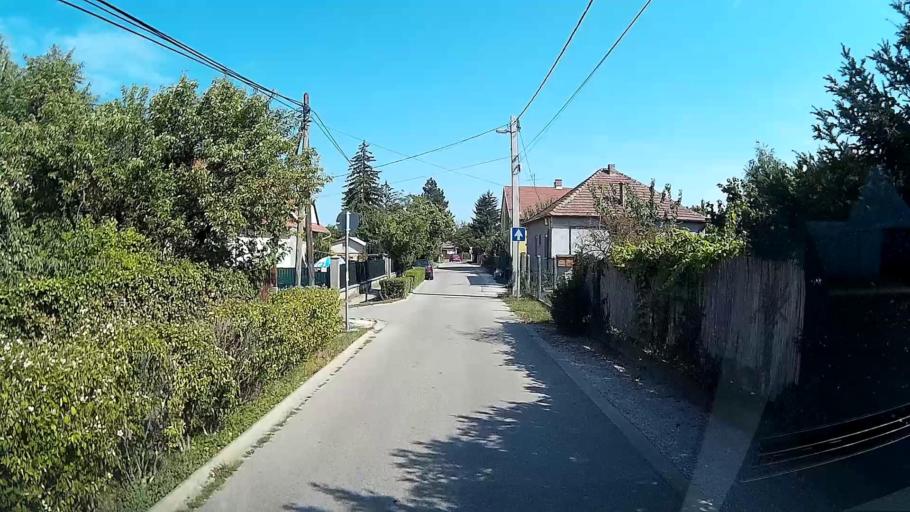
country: HU
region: Pest
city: Pomaz
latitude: 47.6413
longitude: 19.0270
